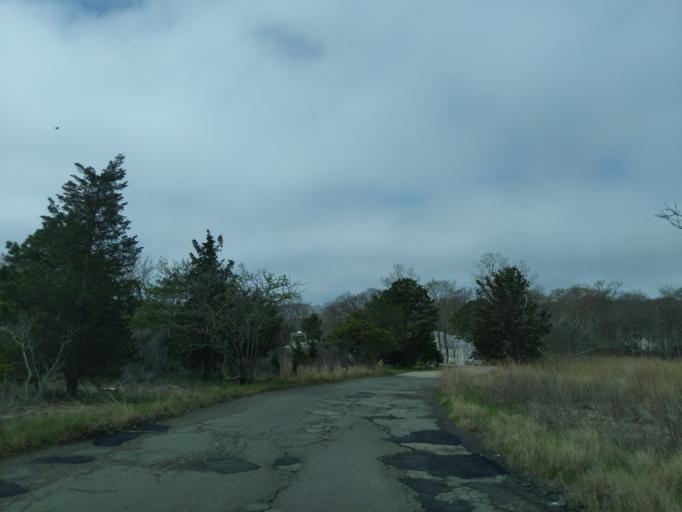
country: US
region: Massachusetts
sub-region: Essex County
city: Rockport
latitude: 42.6295
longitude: -70.6200
